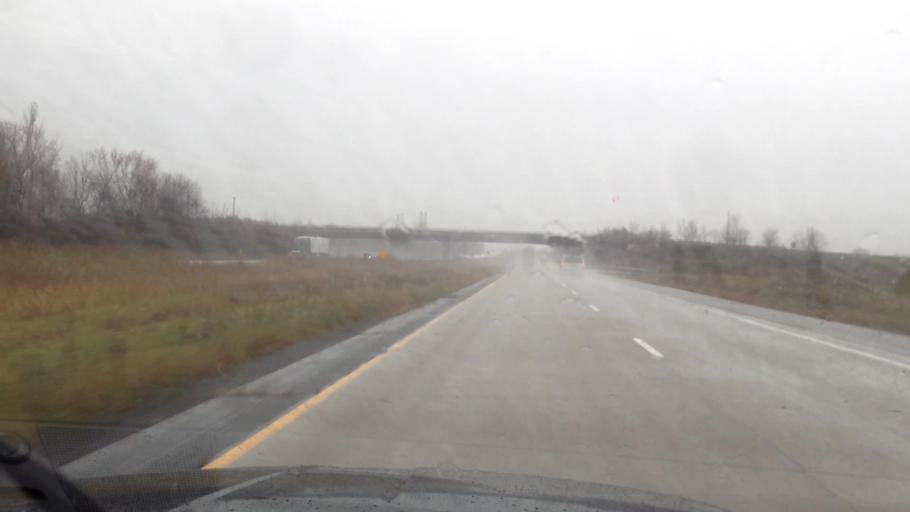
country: CA
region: Ontario
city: Hawkesbury
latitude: 45.5152
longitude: -74.5657
